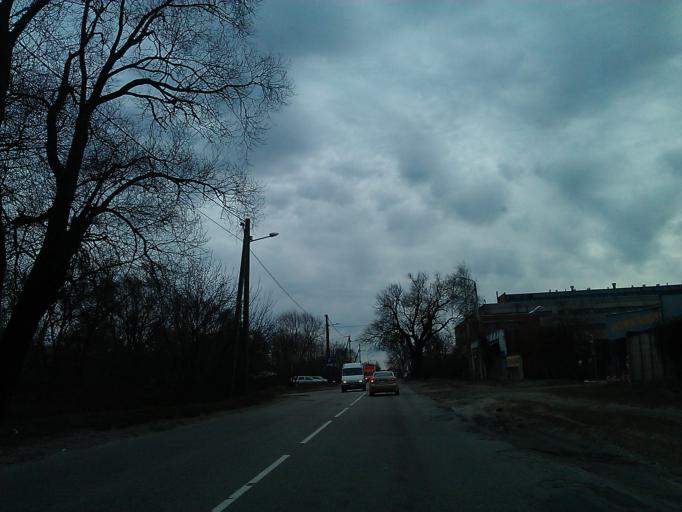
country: LV
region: Riga
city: Riga
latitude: 56.9489
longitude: 24.1635
